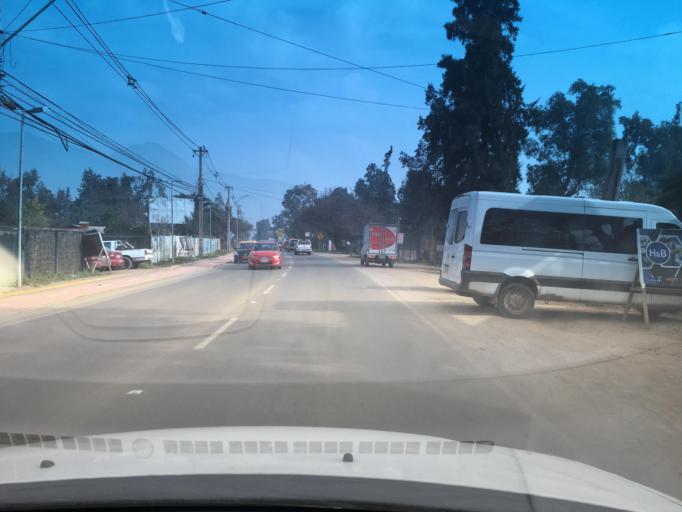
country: CL
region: Santiago Metropolitan
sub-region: Provincia de Chacabuco
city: Lampa
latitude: -33.3008
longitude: -70.8580
